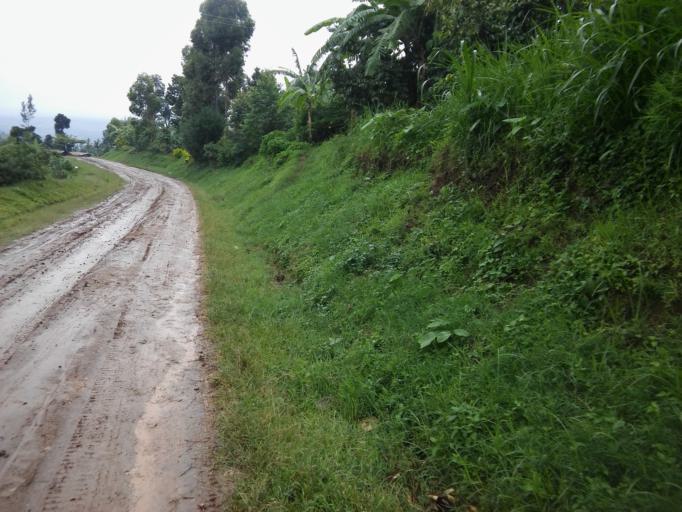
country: UG
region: Eastern Region
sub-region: Mbale District
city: Mbale
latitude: 1.0162
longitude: 34.2232
